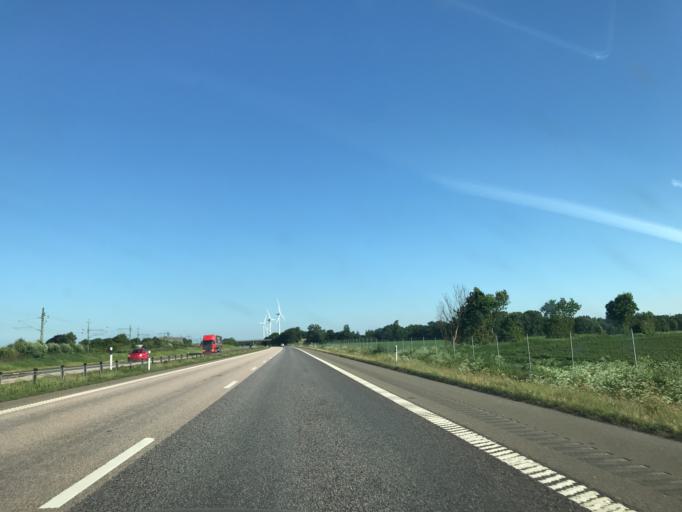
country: SE
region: Halland
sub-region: Varbergs Kommun
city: Tvaaker
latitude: 57.0223
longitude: 12.3907
